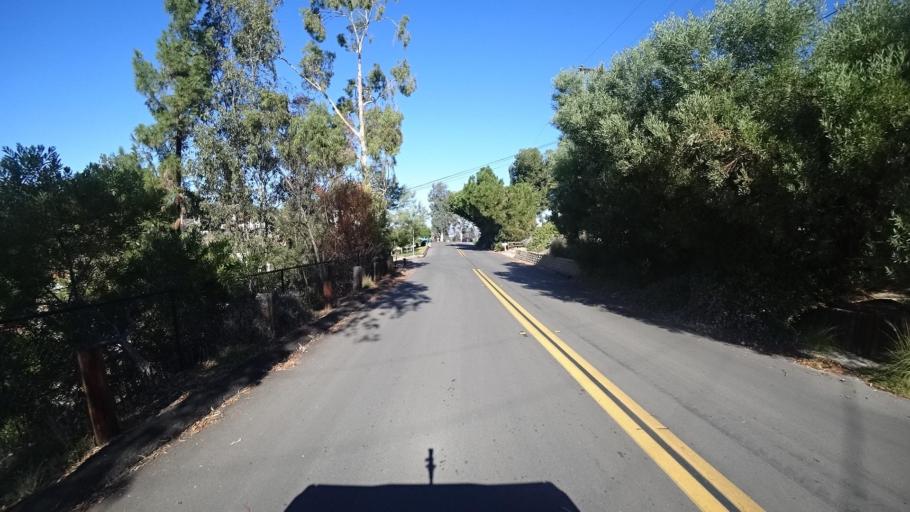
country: US
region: California
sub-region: San Diego County
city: Winter Gardens
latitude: 32.8314
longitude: -116.9271
